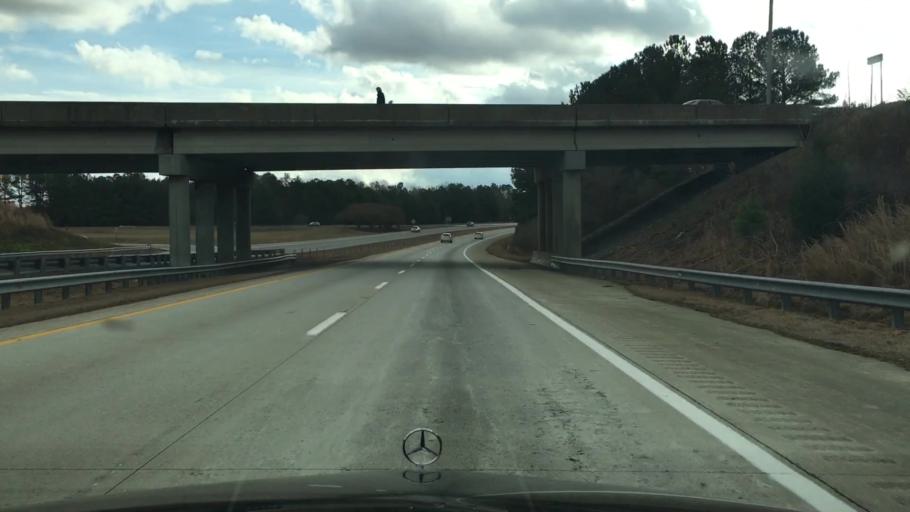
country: US
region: North Carolina
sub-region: Wake County
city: Garner
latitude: 35.6073
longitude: -78.5644
